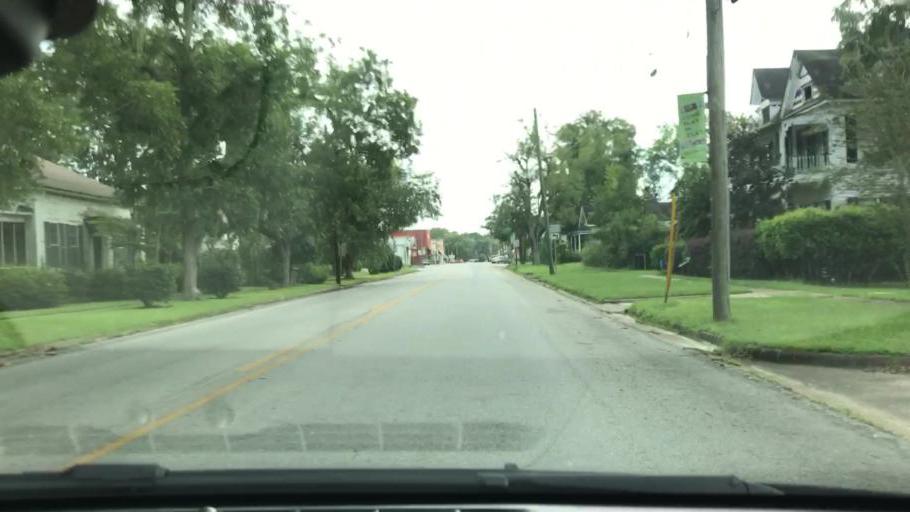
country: US
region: Georgia
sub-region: Clay County
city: Fort Gaines
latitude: 31.6084
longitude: -85.0498
